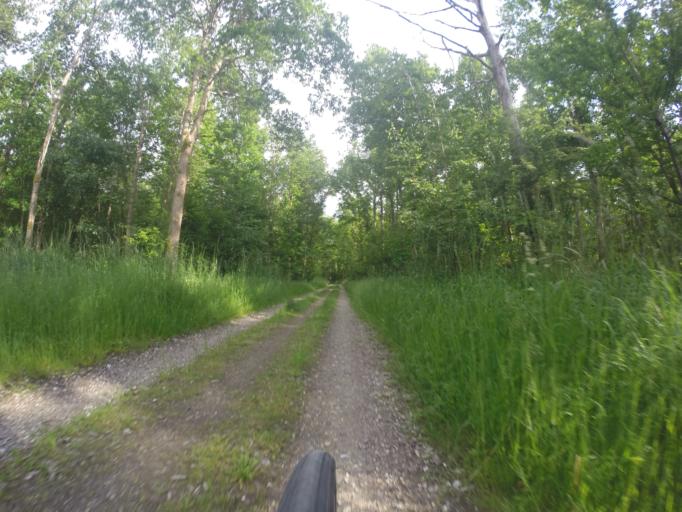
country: DK
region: Capital Region
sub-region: Ballerup Kommune
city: Ballerup
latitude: 55.6988
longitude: 12.3480
